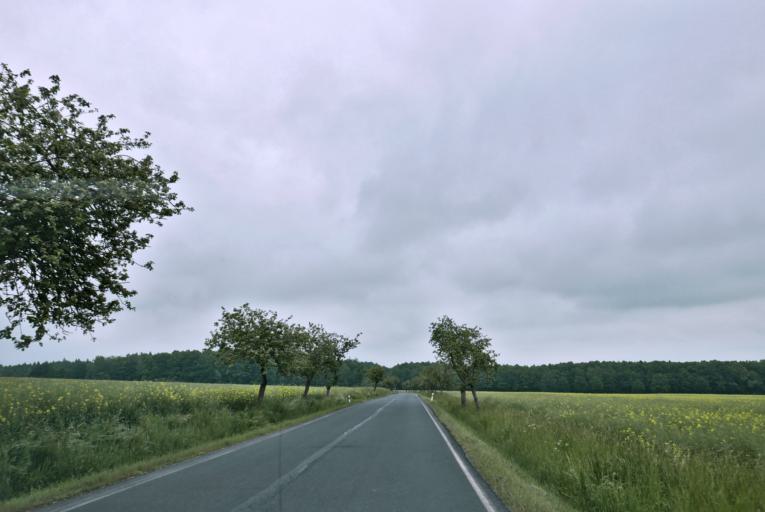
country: CZ
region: Plzensky
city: Plasy
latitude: 49.9856
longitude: 13.4179
